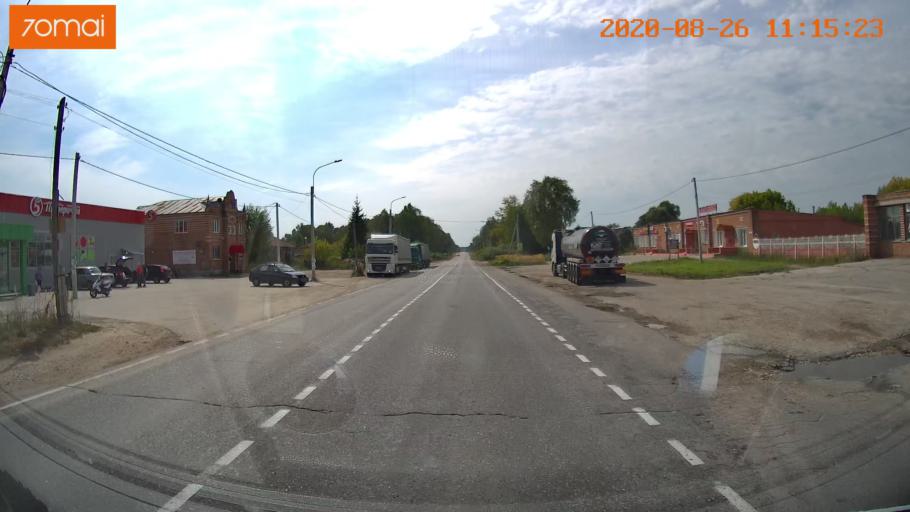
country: RU
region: Rjazan
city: Izhevskoye
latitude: 54.4399
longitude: 41.1148
